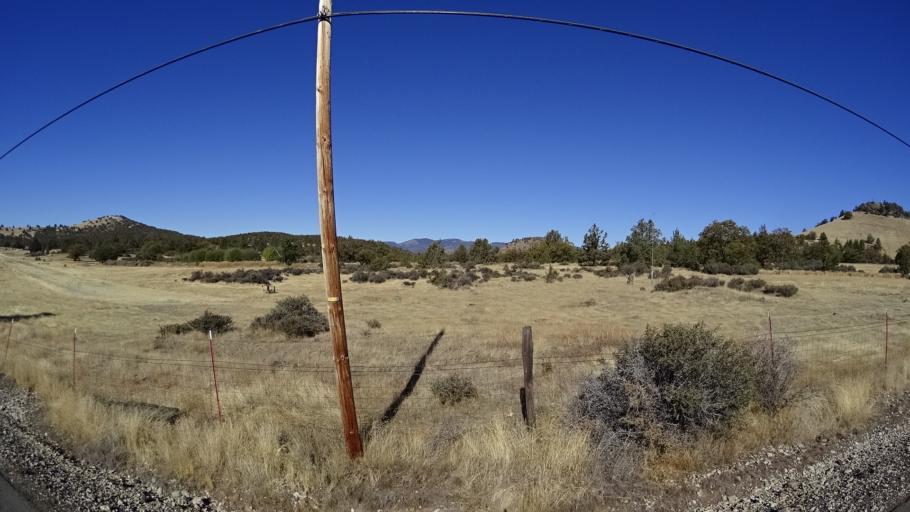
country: US
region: California
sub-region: Siskiyou County
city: Montague
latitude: 41.9539
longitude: -122.3307
